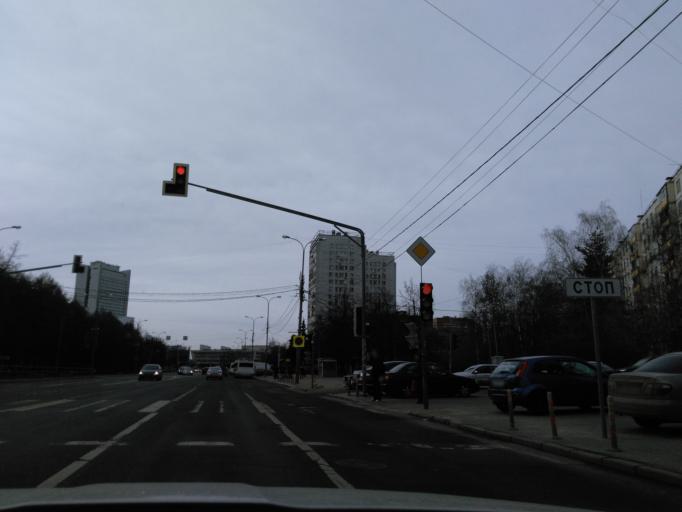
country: RU
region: Moscow
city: Zelenograd
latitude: 55.9959
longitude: 37.2124
